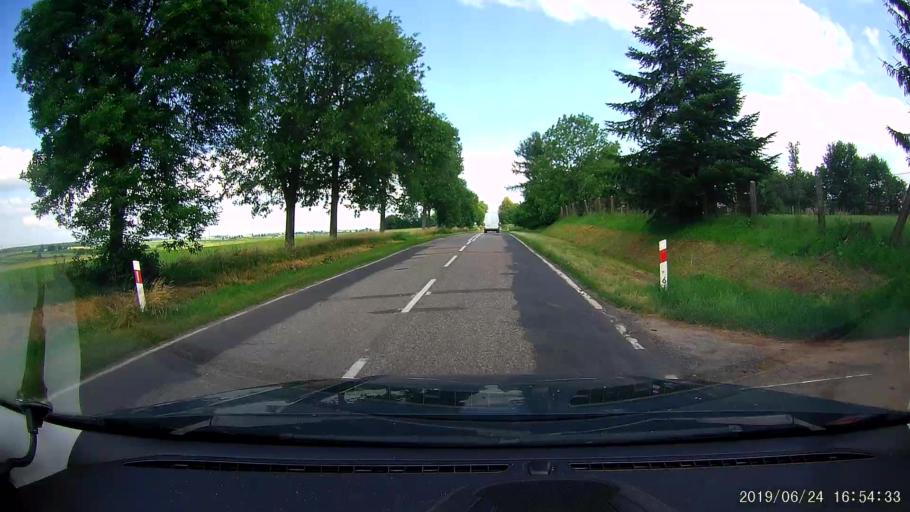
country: PL
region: Lublin Voivodeship
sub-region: Powiat tomaszowski
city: Telatyn
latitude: 50.5314
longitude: 23.8160
